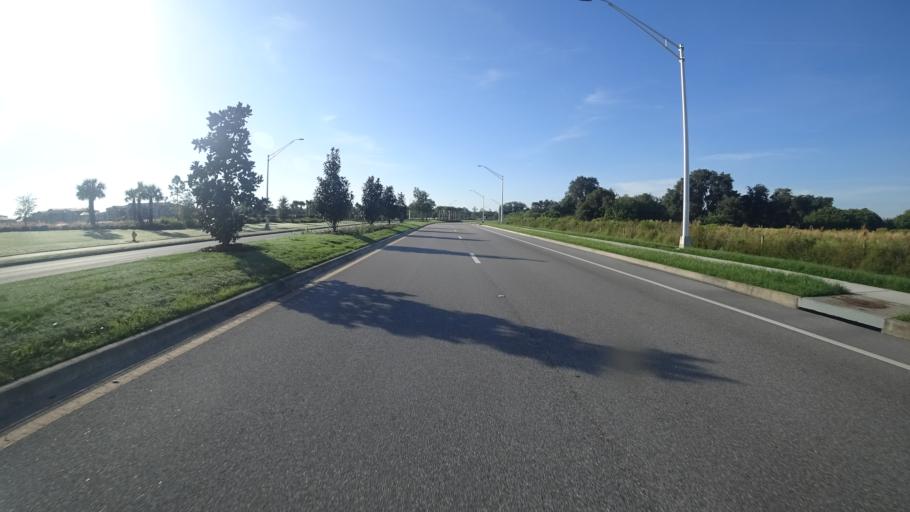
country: US
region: Florida
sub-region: Sarasota County
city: The Meadows
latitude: 27.4313
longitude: -82.3730
